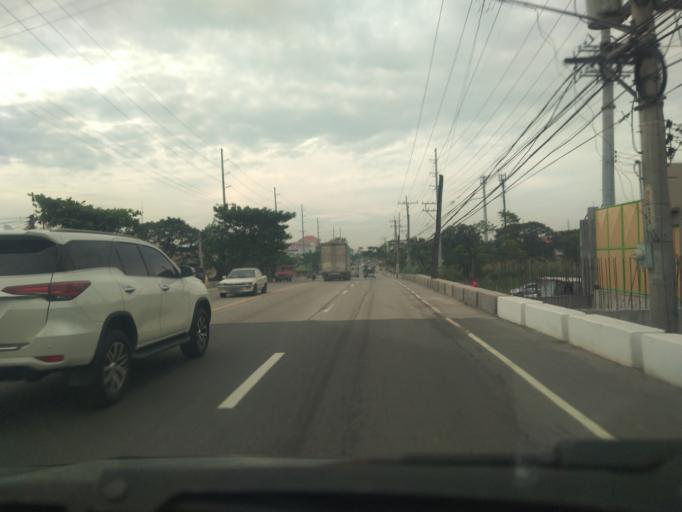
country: PH
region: Central Luzon
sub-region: Province of Pampanga
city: San Fernando
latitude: 15.0274
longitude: 120.6973
